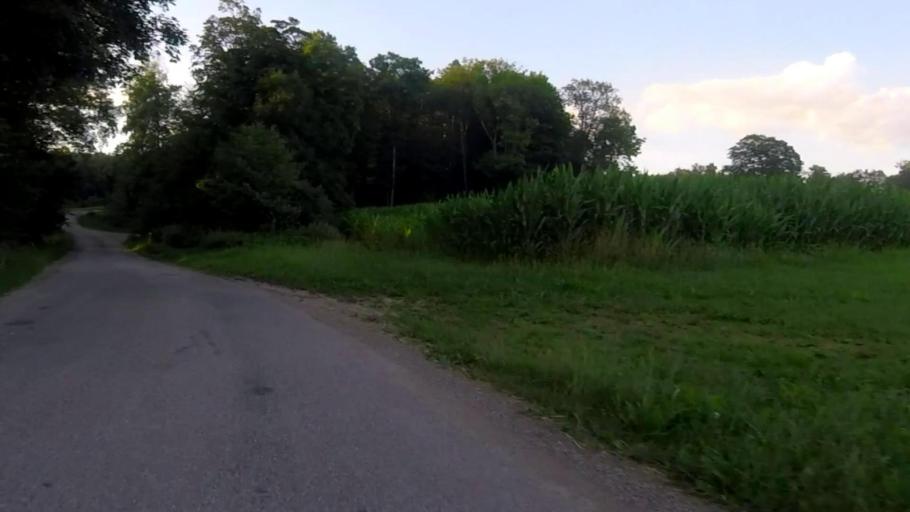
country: DE
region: Baden-Wuerttemberg
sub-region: Regierungsbezirk Stuttgart
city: Oppenweiler
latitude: 49.0006
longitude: 9.4606
